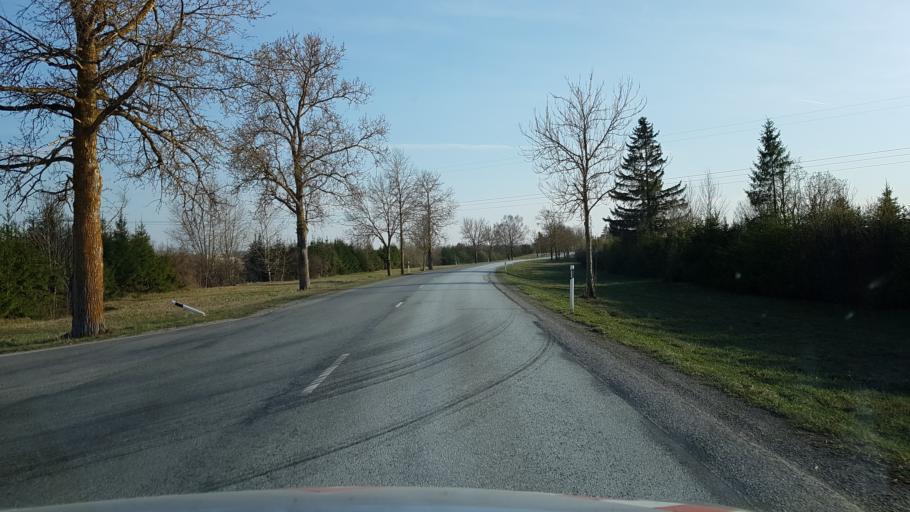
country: EE
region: Laeaene-Virumaa
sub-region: Rakvere linn
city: Rakvere
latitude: 59.3795
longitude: 26.3917
